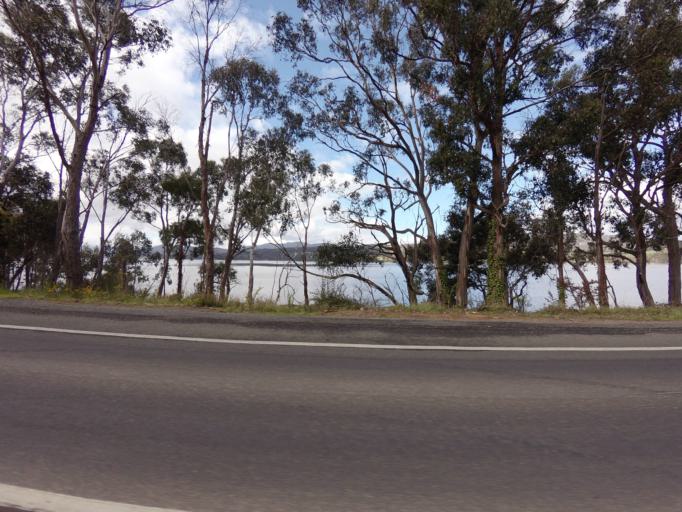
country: AU
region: Tasmania
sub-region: Huon Valley
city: Geeveston
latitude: -43.1504
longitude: 146.9801
